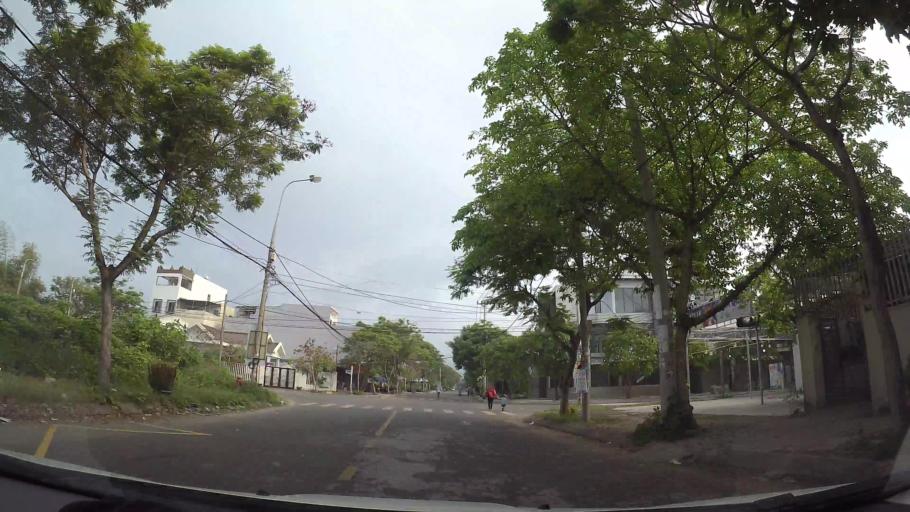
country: VN
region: Da Nang
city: Son Tra
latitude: 16.0866
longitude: 108.2465
